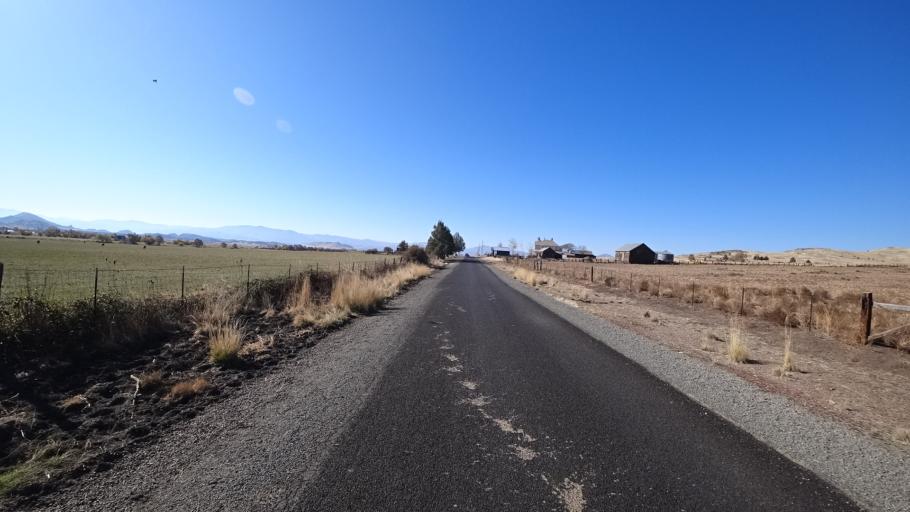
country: US
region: California
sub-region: Siskiyou County
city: Montague
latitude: 41.7262
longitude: -122.3787
